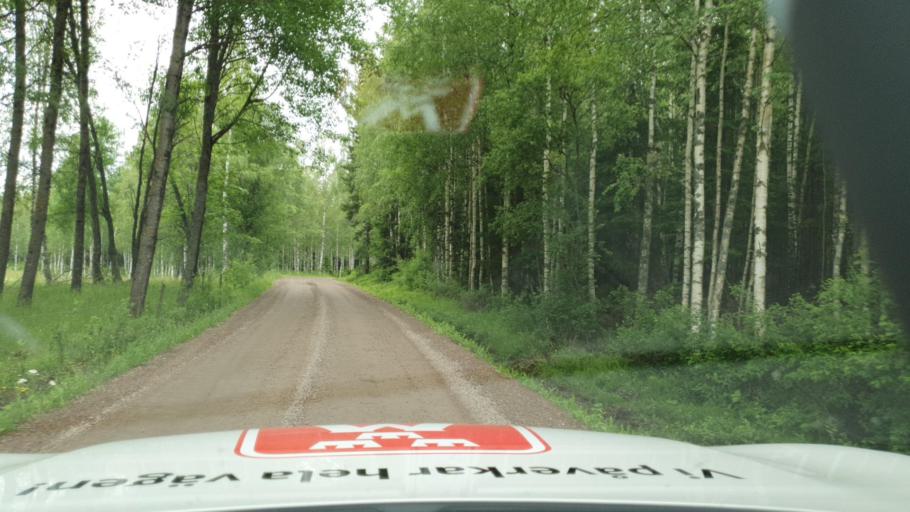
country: SE
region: Vaermland
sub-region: Filipstads Kommun
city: Filipstad
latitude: 59.5773
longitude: 13.9569
